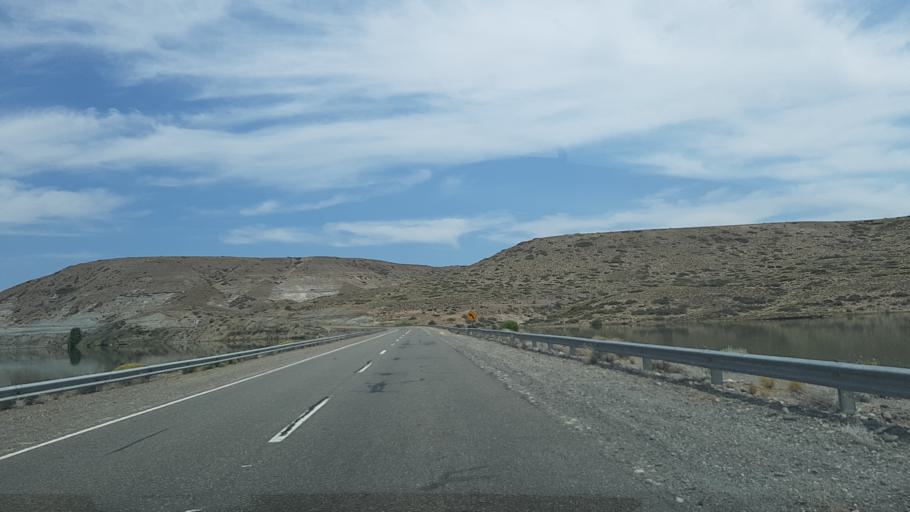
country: AR
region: Neuquen
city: Junin de los Andes
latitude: -40.4383
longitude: -70.6569
